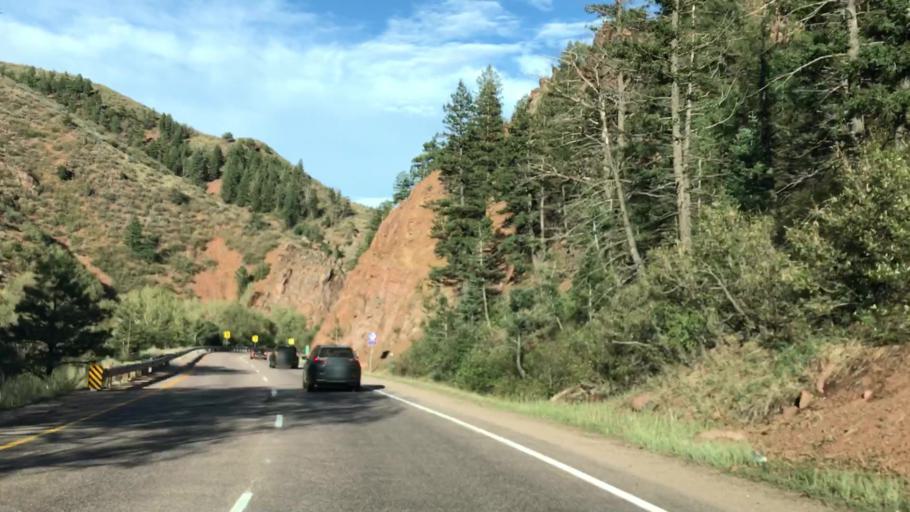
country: US
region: Colorado
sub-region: El Paso County
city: Manitou Springs
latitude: 38.8781
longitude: -104.9438
